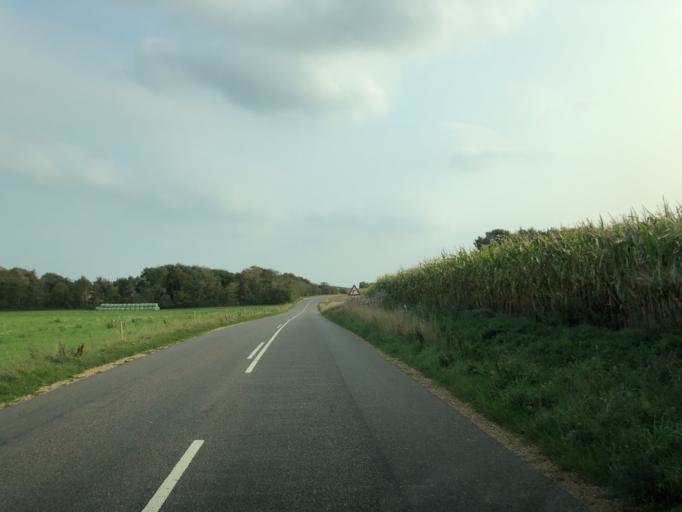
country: DK
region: Central Jutland
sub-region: Ringkobing-Skjern Kommune
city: Videbaek
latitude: 56.0801
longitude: 8.7049
